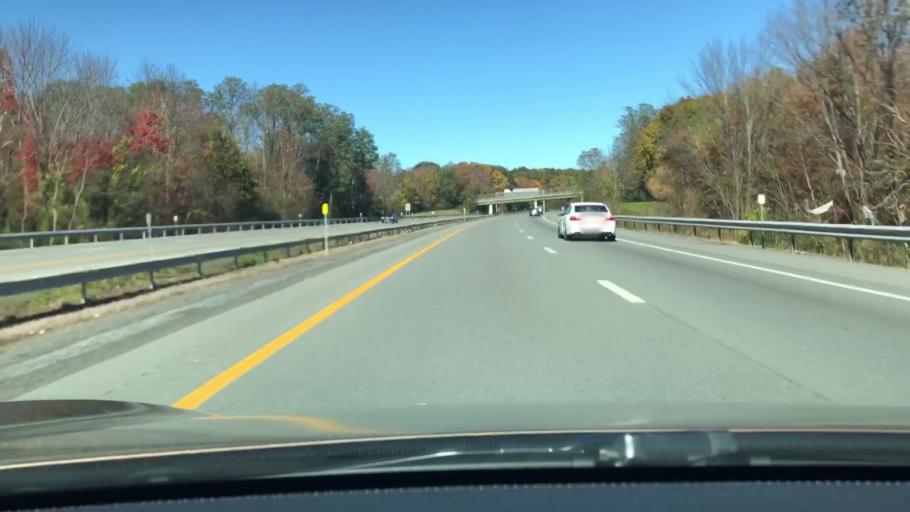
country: US
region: New York
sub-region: Orange County
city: Central Valley
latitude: 41.3399
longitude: -74.1171
